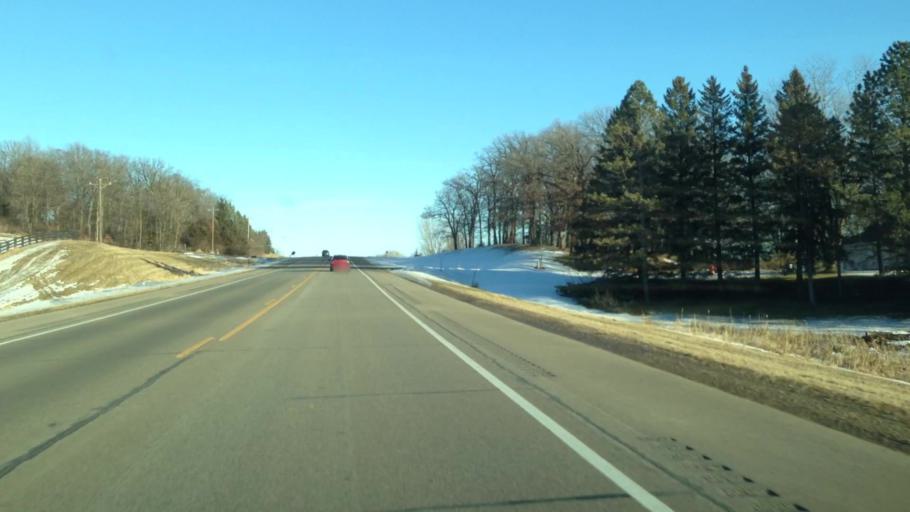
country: US
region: Minnesota
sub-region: Rice County
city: Lonsdale
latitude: 44.4791
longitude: -93.3652
